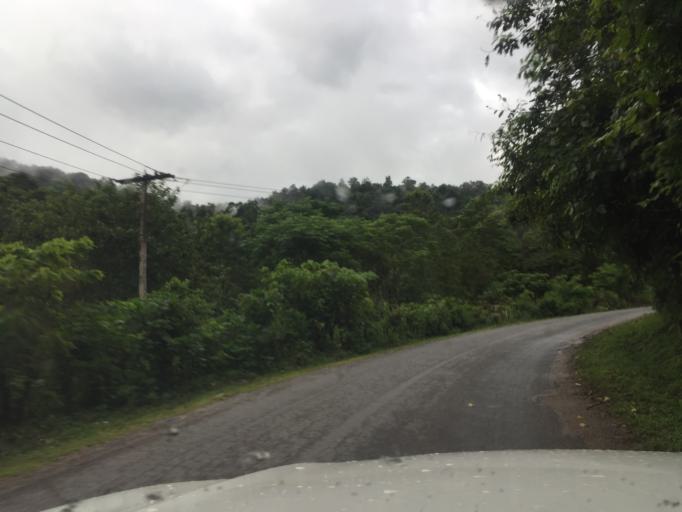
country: LA
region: Oudomxai
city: Muang La
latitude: 20.8670
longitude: 102.1305
